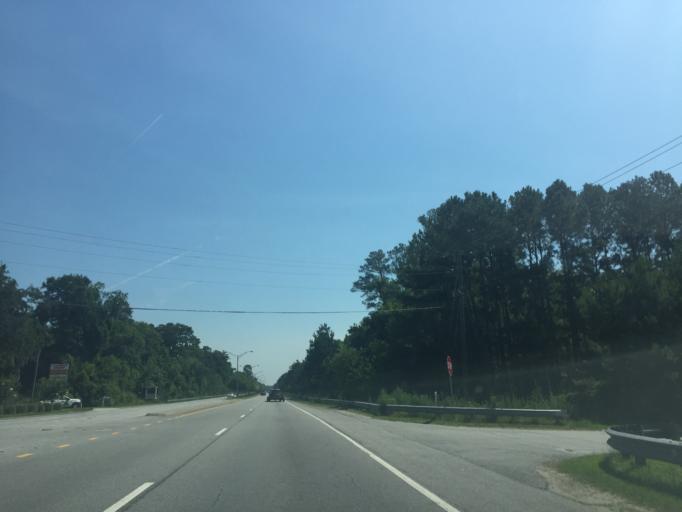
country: US
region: Georgia
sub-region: Bryan County
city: Richmond Hill
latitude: 31.9567
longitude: -81.3068
